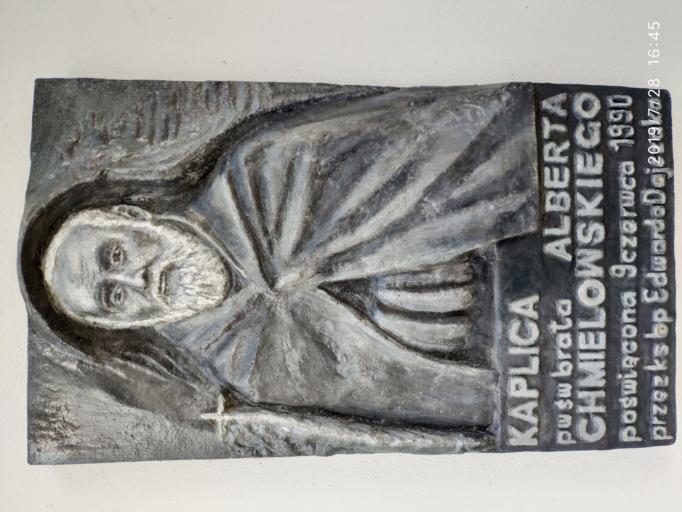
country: PL
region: Lubusz
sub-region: Powiat swiebodzinski
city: Miedzylesie
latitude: 52.1459
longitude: 15.4091
